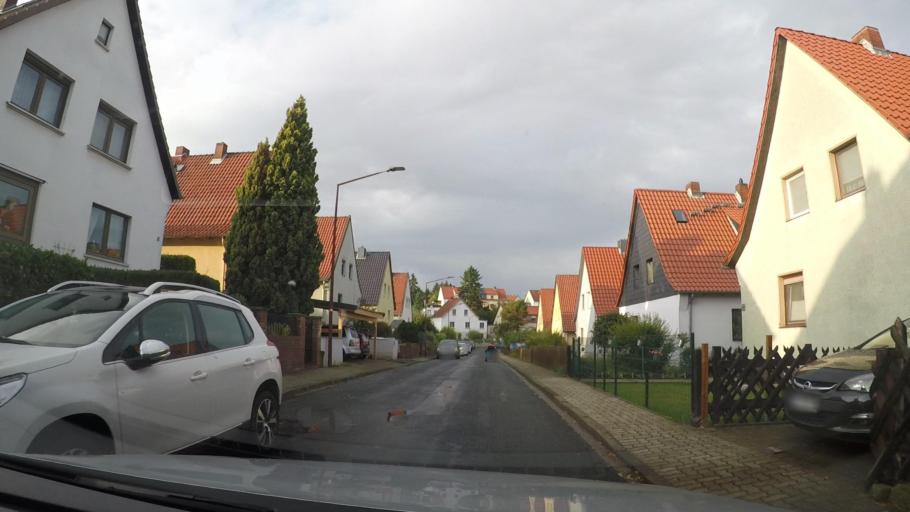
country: DE
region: Lower Saxony
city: Schoningen
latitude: 52.1325
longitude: 10.9601
